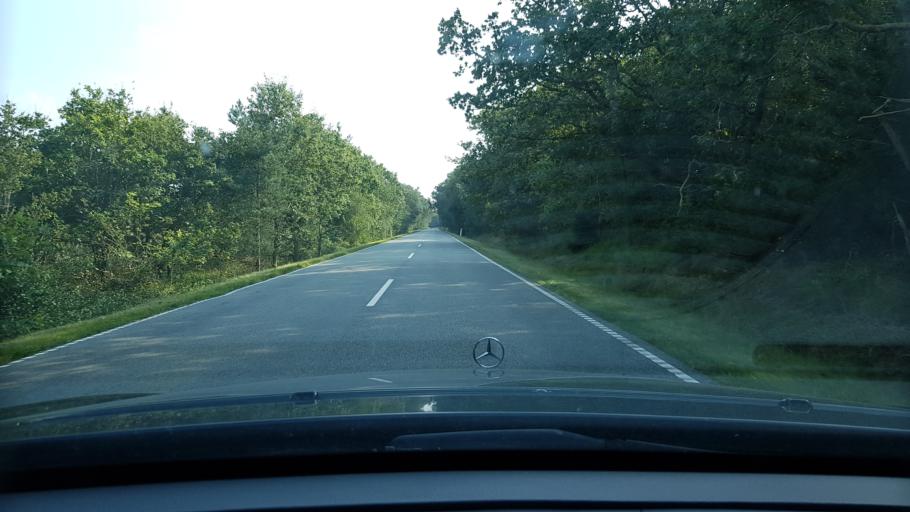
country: DK
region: North Denmark
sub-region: Alborg Kommune
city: Hals
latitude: 56.8598
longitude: 10.2629
